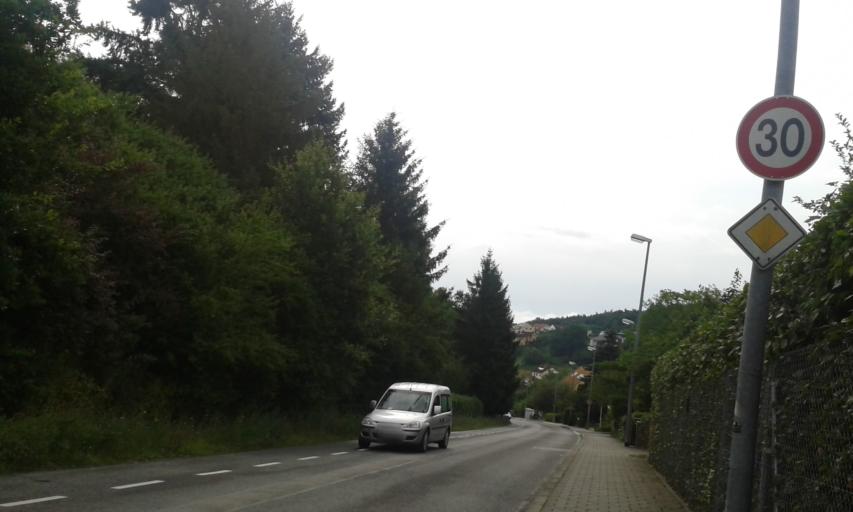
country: DE
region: Bavaria
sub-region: Upper Franconia
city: Bamberg
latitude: 49.8710
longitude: 10.8927
